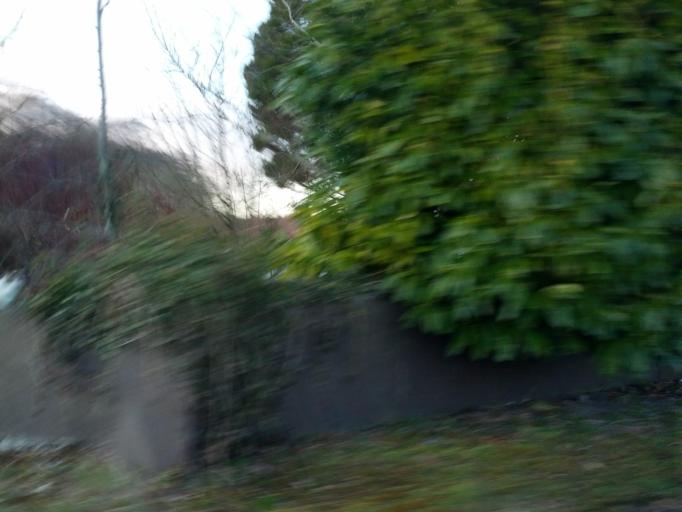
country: IE
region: Connaught
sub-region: County Galway
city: Athenry
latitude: 53.2799
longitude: -8.7509
